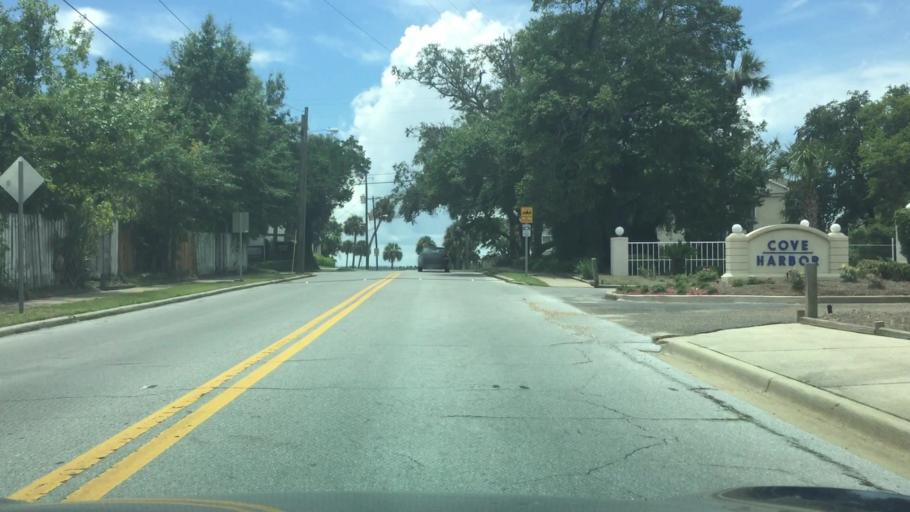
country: US
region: Florida
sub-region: Bay County
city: Panama City
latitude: 30.1501
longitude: -85.6589
